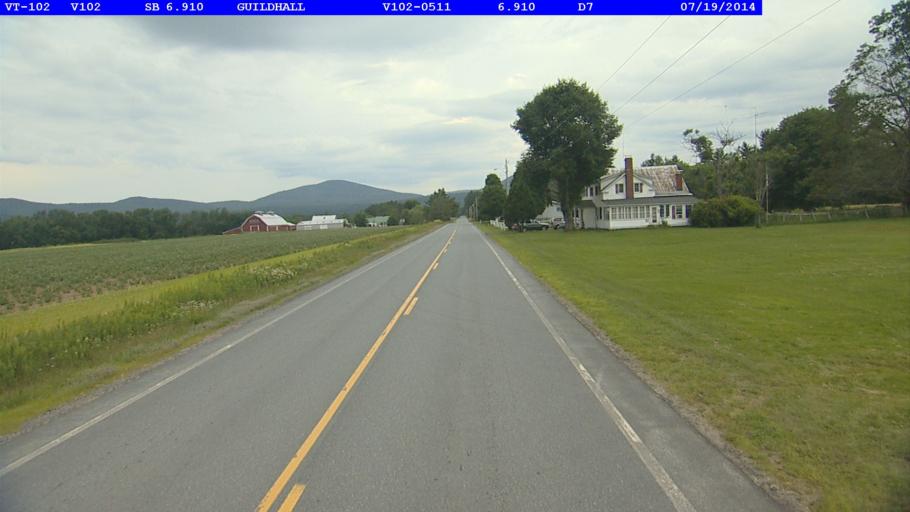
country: US
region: Vermont
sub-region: Essex County
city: Guildhall
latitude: 44.5653
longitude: -71.5671
